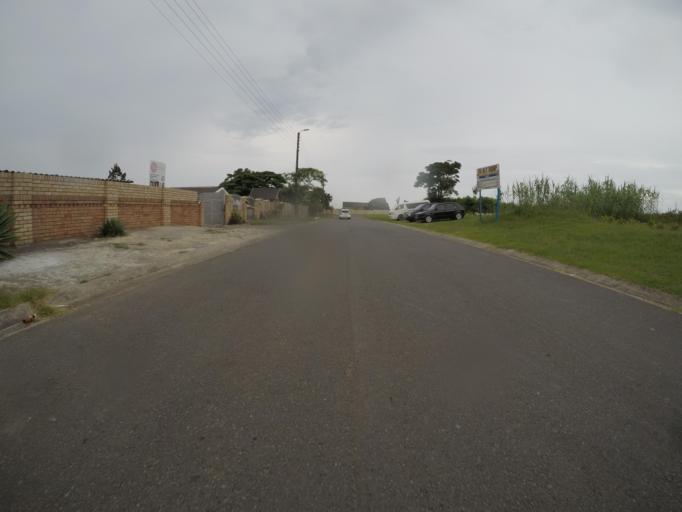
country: ZA
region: Eastern Cape
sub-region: Buffalo City Metropolitan Municipality
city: East London
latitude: -32.9992
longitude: 27.8501
